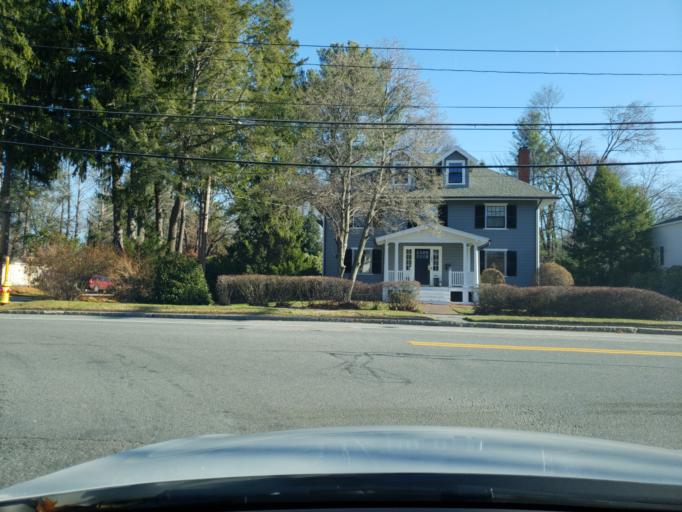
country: US
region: Massachusetts
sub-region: Essex County
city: Andover
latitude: 42.6423
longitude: -71.1316
